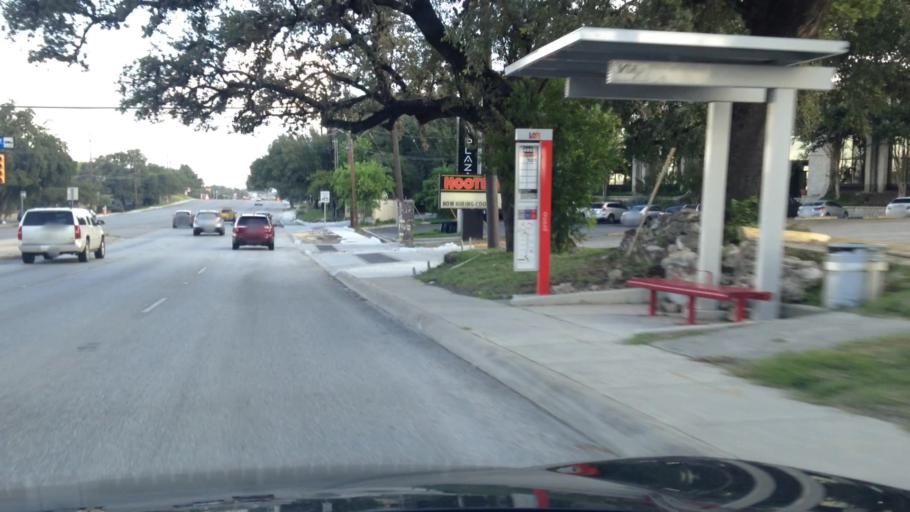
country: US
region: Texas
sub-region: Bexar County
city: Balcones Heights
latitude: 29.5211
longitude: -98.5735
